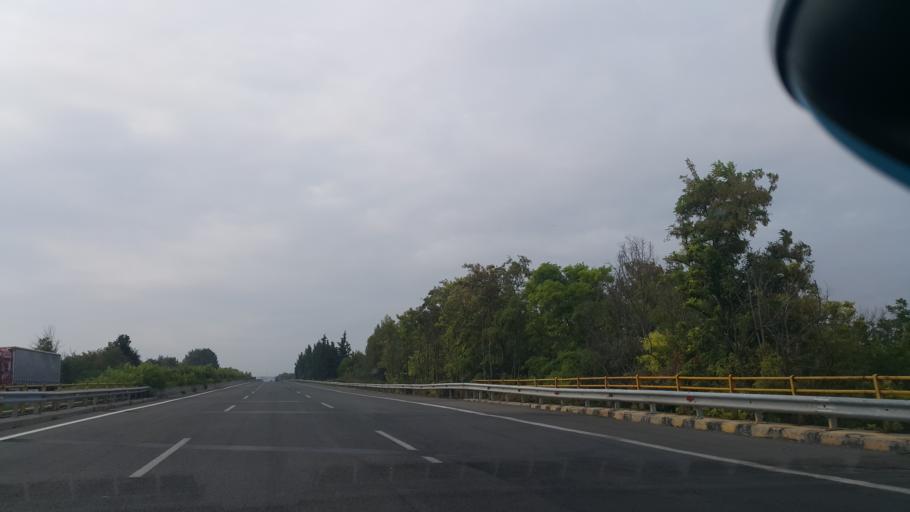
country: GR
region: Central Macedonia
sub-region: Nomos Pierias
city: Aiginio
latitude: 40.4877
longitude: 22.5656
